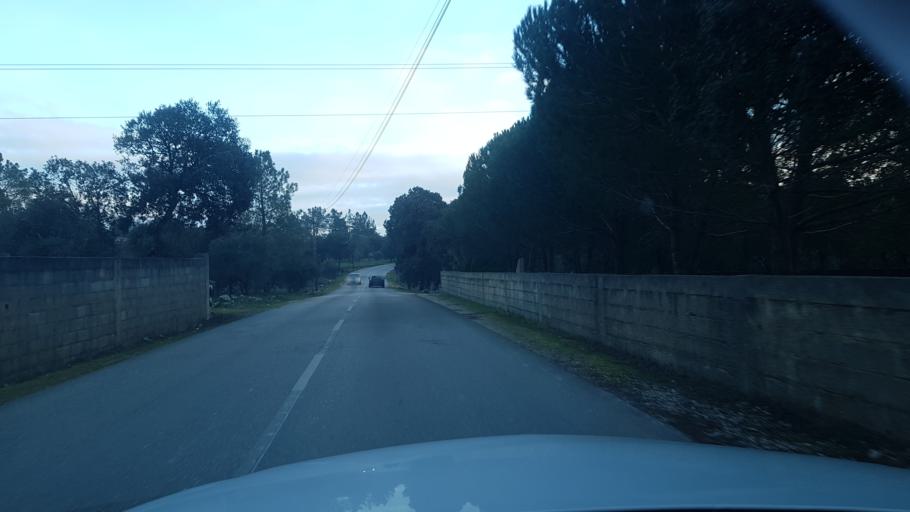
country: PT
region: Santarem
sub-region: Ourem
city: Fatima
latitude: 39.5988
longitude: -8.6508
